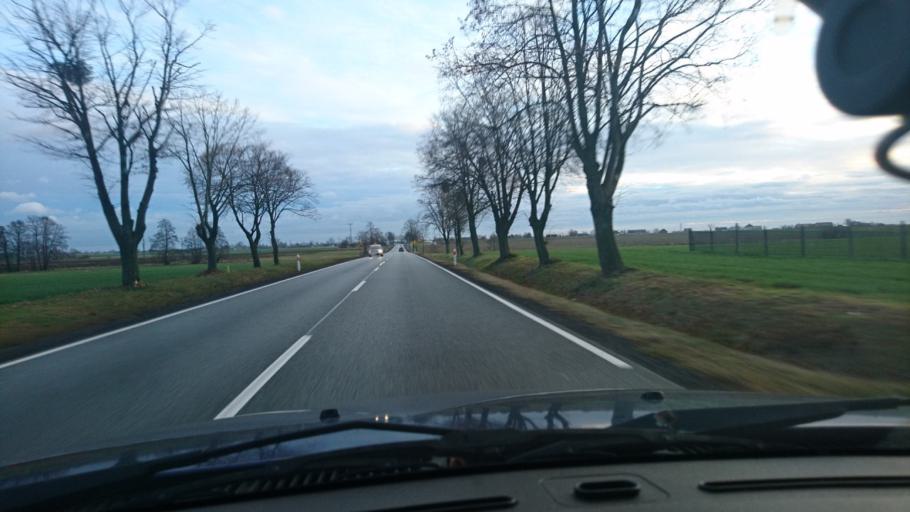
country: PL
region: Opole Voivodeship
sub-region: Powiat kluczborski
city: Kluczbork
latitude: 51.0191
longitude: 18.1972
